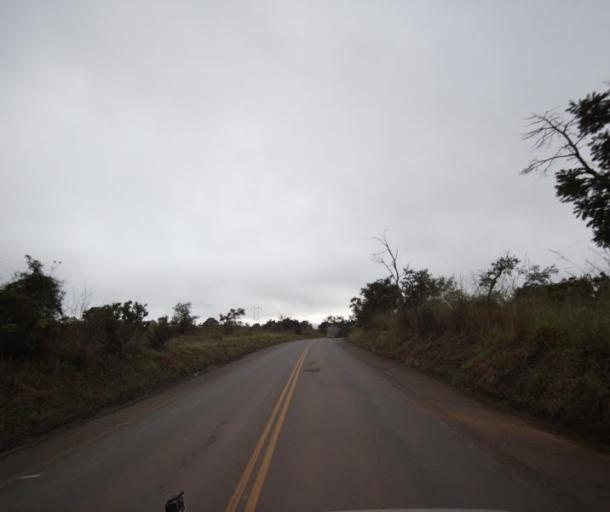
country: BR
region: Goias
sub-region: Pirenopolis
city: Pirenopolis
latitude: -15.8710
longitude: -48.7812
